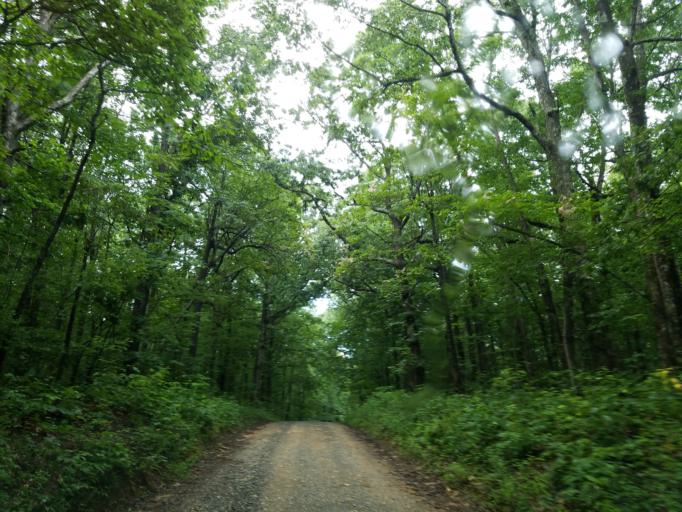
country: US
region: Georgia
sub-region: Lumpkin County
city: Dahlonega
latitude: 34.6475
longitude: -84.1573
